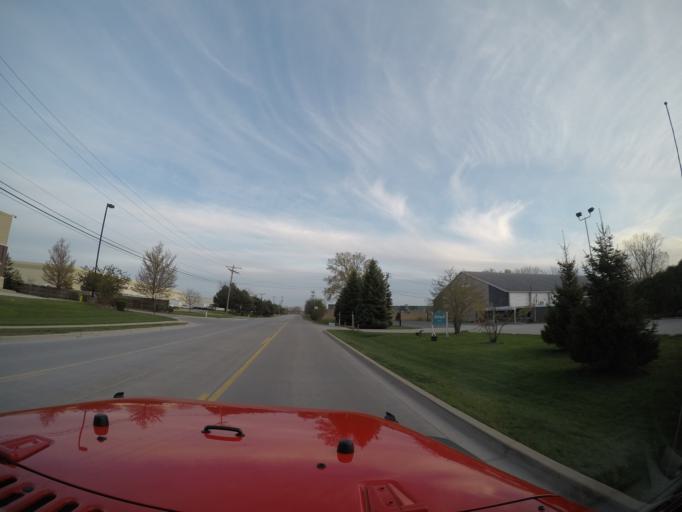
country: US
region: Illinois
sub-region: Cook County
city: Northbrook
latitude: 42.1018
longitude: -87.8149
